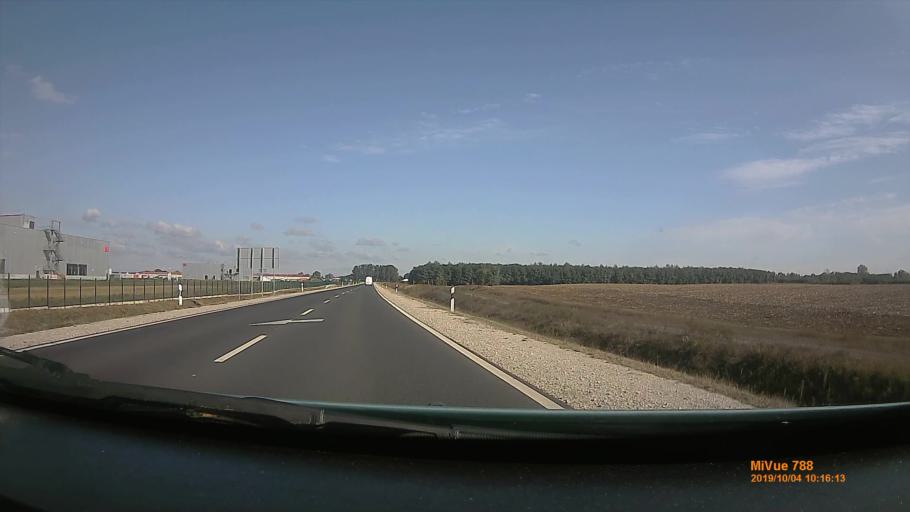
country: HU
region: Szabolcs-Szatmar-Bereg
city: Nyiregyhaza
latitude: 47.9468
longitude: 21.6525
